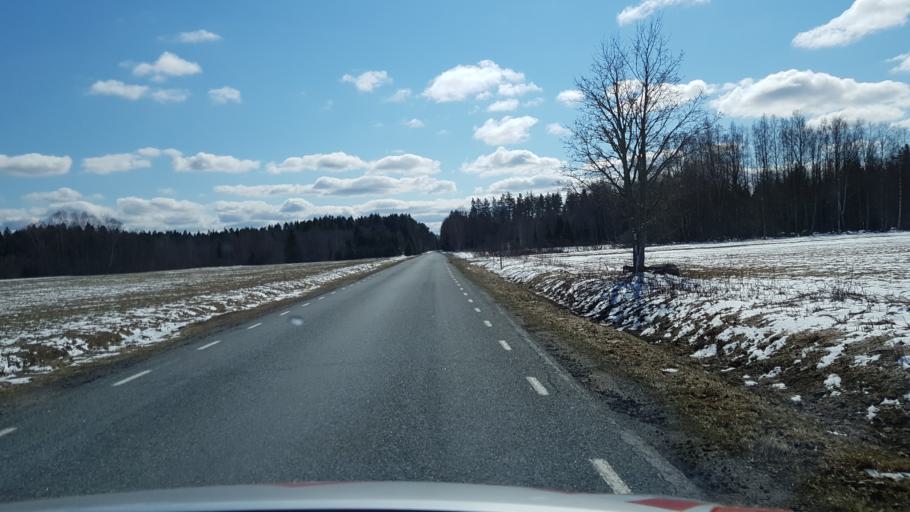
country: EE
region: Laeaene-Virumaa
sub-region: Kadrina vald
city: Kadrina
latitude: 59.4935
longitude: 25.9808
